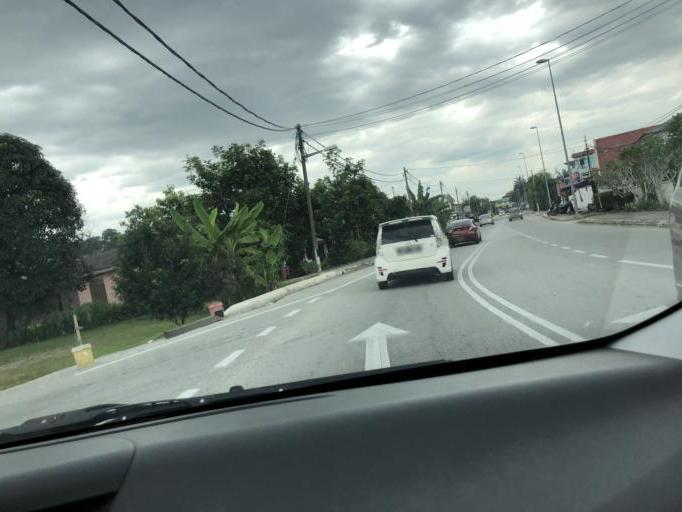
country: MY
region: Putrajaya
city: Putrajaya
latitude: 2.9235
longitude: 101.7594
